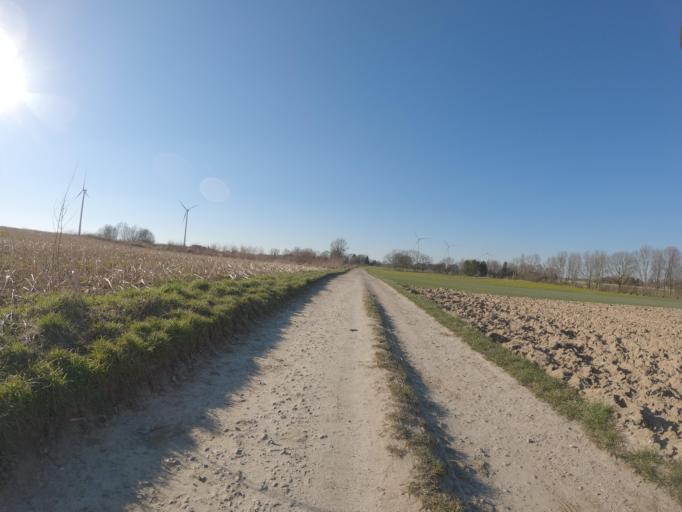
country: NL
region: Limburg
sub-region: Gemeente Kerkrade
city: Kerkrade
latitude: 50.8256
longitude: 6.0408
